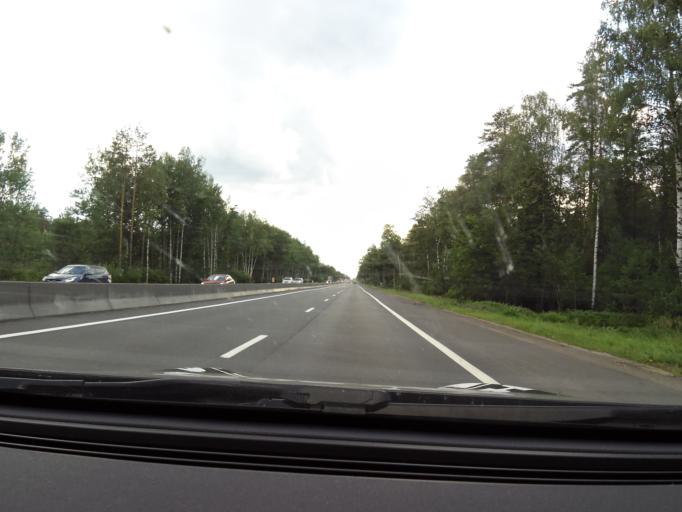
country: RU
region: Nizjnij Novgorod
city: Yuganets
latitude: 56.2890
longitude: 43.2518
